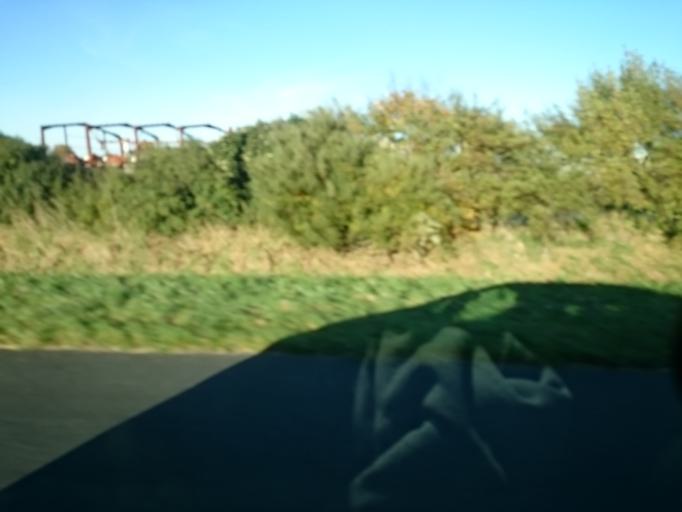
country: FR
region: Brittany
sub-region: Departement des Cotes-d'Armor
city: Plestan
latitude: 48.4155
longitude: -2.4330
